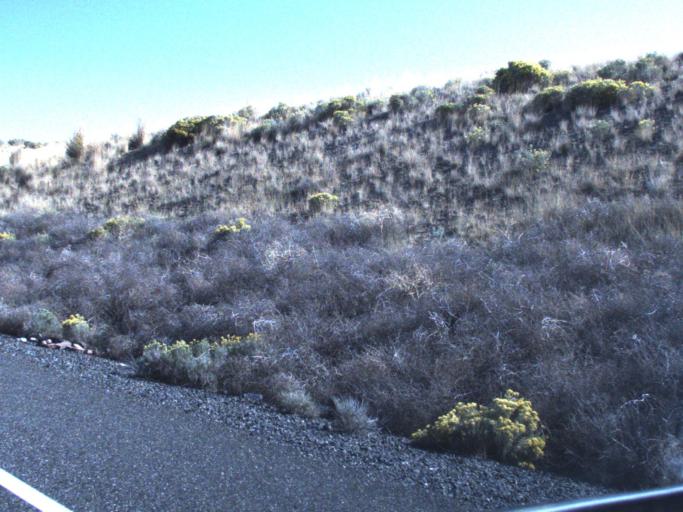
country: US
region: Washington
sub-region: Benton County
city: Highland
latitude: 46.1499
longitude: -119.1262
